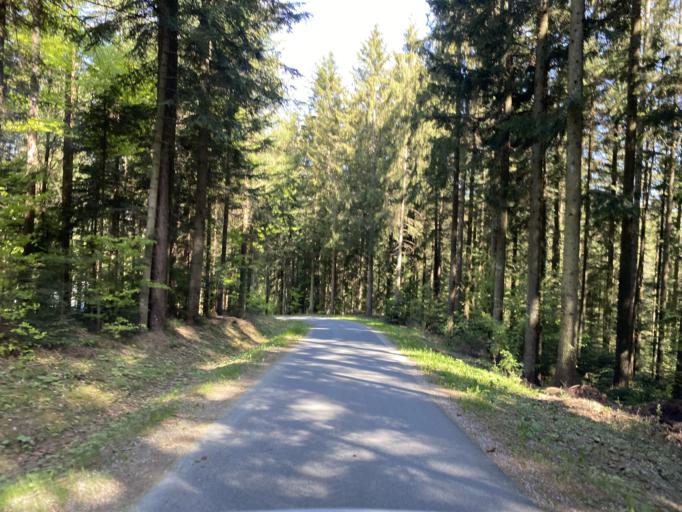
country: AT
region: Styria
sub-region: Politischer Bezirk Weiz
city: Birkfeld
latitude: 47.3687
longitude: 15.6997
